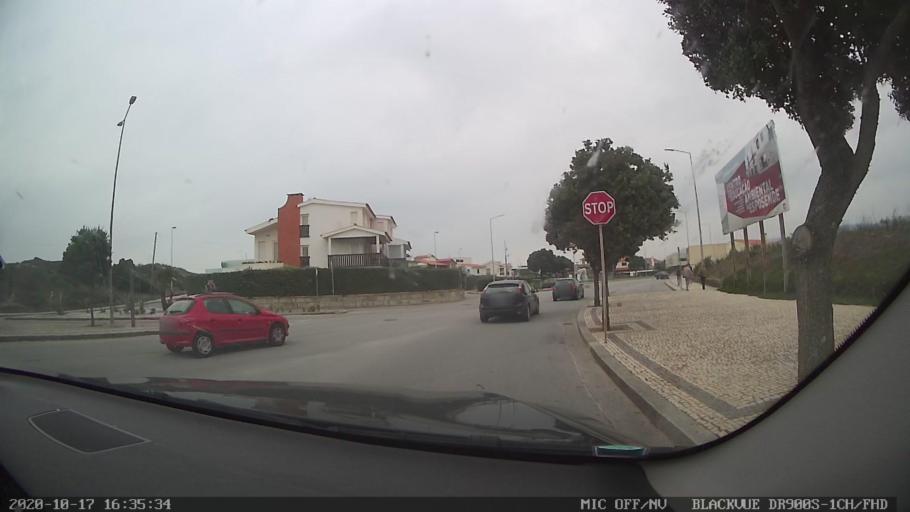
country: PT
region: Braga
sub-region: Esposende
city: Esposende
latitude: 41.5430
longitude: -8.7911
